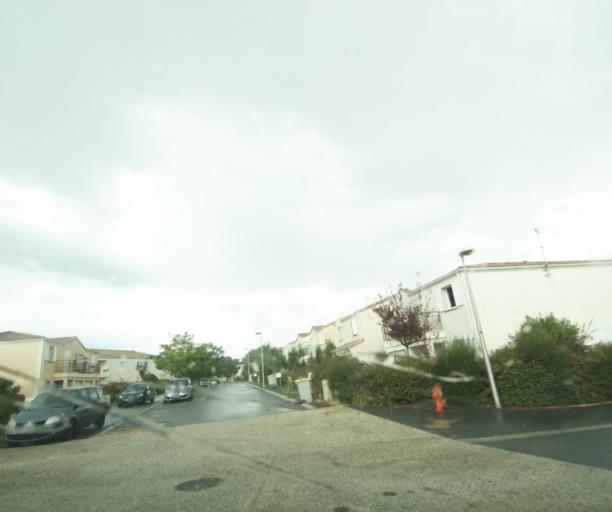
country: FR
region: Poitou-Charentes
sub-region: Departement de la Charente-Maritime
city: Tonnay-Charente
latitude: 45.9486
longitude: -0.8757
